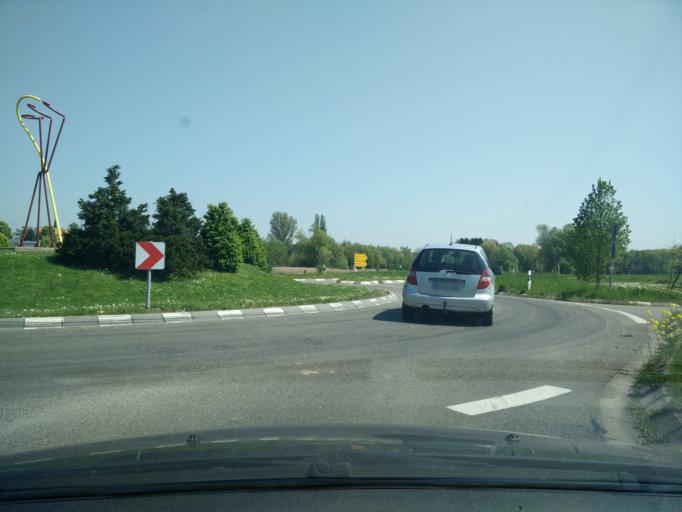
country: DE
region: Rheinland-Pfalz
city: Barbelroth
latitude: 49.0978
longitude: 8.0669
